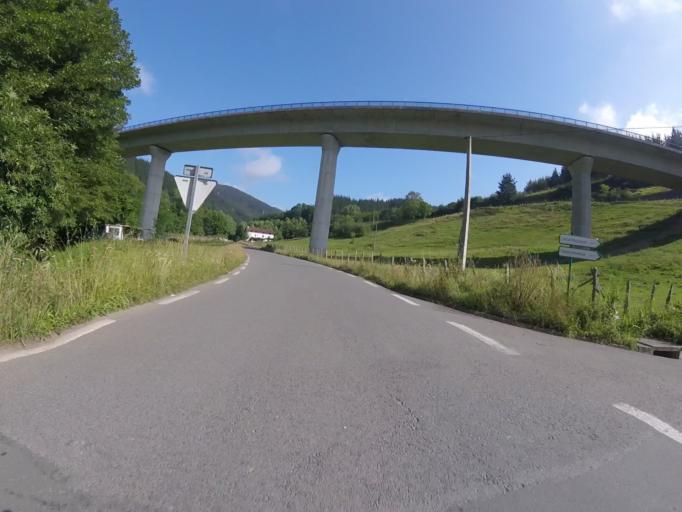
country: ES
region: Basque Country
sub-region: Provincia de Guipuzcoa
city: Ormaiztegui
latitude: 43.0536
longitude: -2.2342
